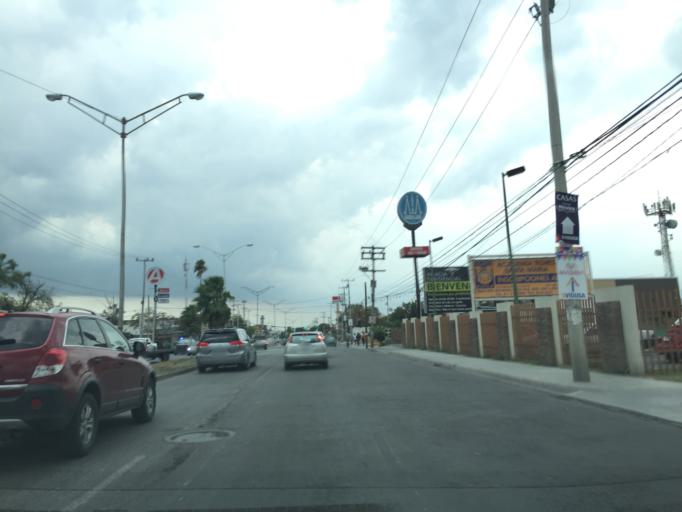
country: MX
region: Nuevo Leon
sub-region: Juarez
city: Valle de Juarez
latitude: 25.6592
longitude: -100.1800
